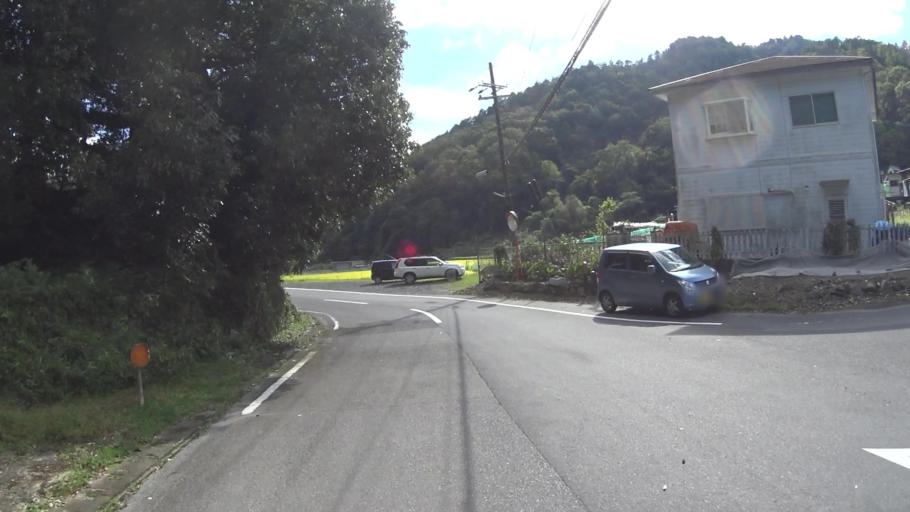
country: JP
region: Kyoto
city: Uji
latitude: 34.9328
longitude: 135.8575
